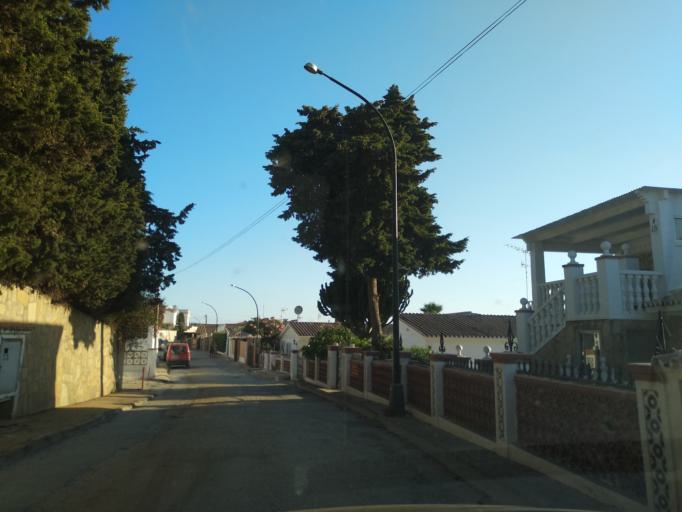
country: ES
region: Andalusia
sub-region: Provincia de Malaga
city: Valdes
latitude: 36.7195
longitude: -4.1914
